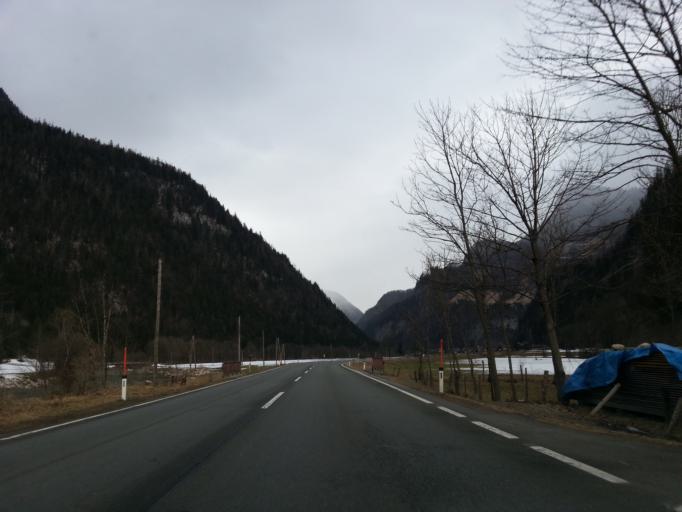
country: AT
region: Salzburg
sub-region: Politischer Bezirk Zell am See
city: Leogang
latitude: 47.5094
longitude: 12.7620
